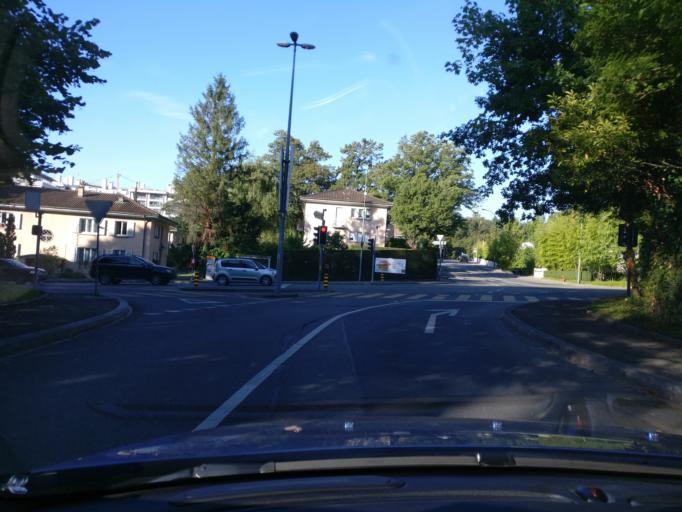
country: CH
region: Geneva
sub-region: Geneva
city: Le Grand-Saconnex
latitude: 46.2246
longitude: 6.1342
